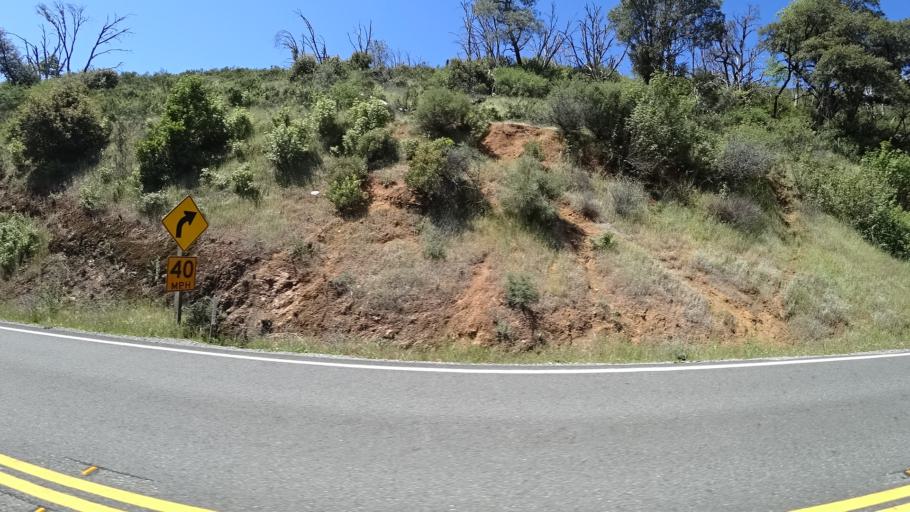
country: US
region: California
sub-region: Trinity County
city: Weaverville
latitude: 40.7364
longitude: -123.0087
